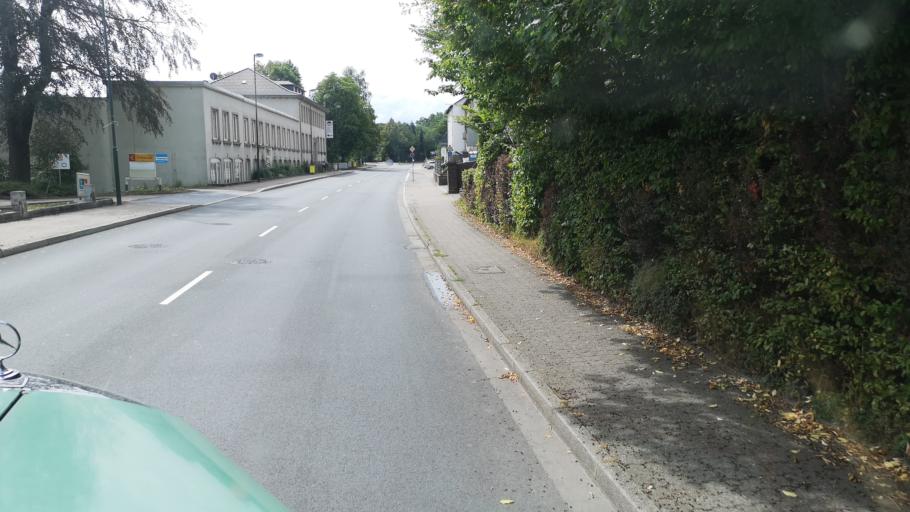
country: DE
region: North Rhine-Westphalia
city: Huckeswagen
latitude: 51.1446
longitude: 7.3505
